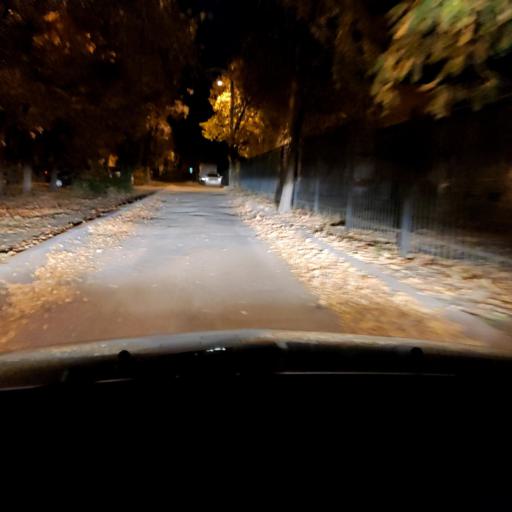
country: RU
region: Voronezj
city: Voronezh
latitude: 51.6542
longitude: 39.1552
